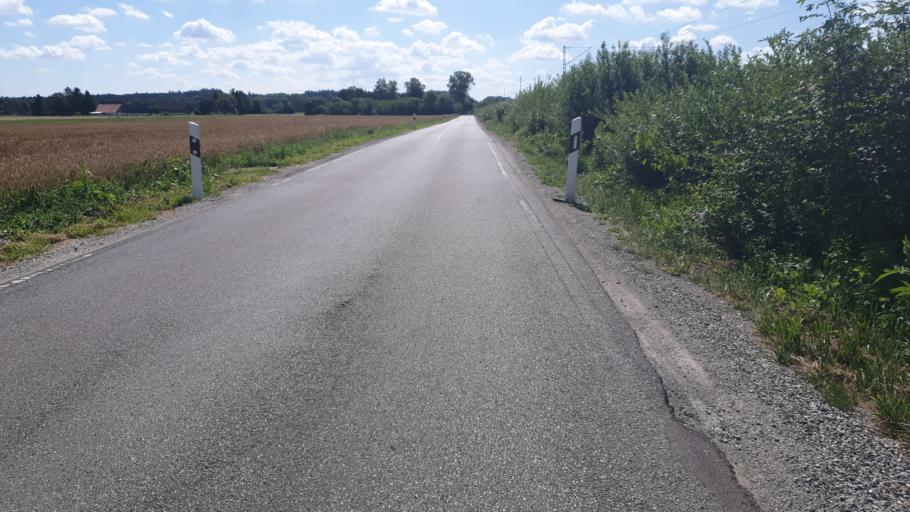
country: DE
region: Bavaria
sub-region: Upper Bavaria
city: Puchheim
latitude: 48.1678
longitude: 11.3688
